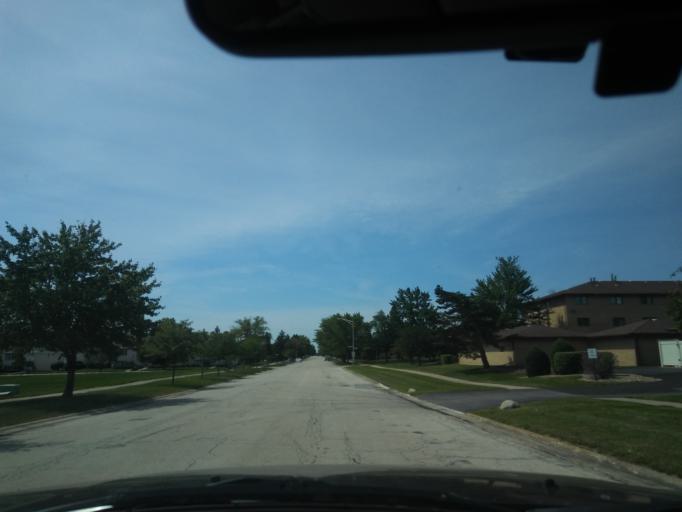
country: US
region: Illinois
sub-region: Cook County
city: Tinley Park
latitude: 41.6161
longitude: -87.7968
